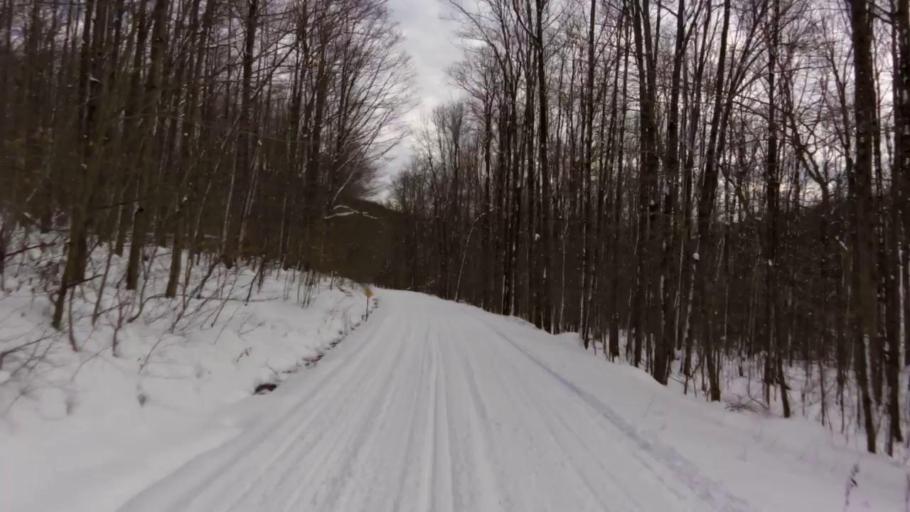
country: US
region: New York
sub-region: Cattaraugus County
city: Salamanca
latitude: 42.0531
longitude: -78.7560
